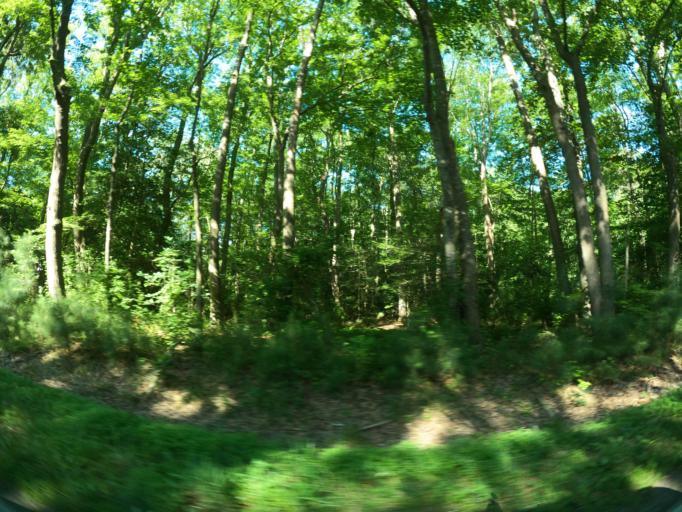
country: US
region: Delaware
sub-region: Sussex County
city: Ocean View
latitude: 38.4790
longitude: -75.1174
